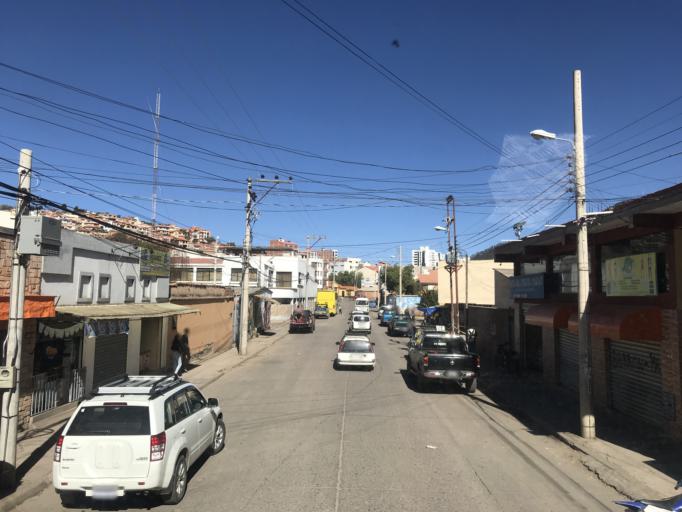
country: BO
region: Chuquisaca
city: Sucre
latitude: -19.0387
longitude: -65.2446
